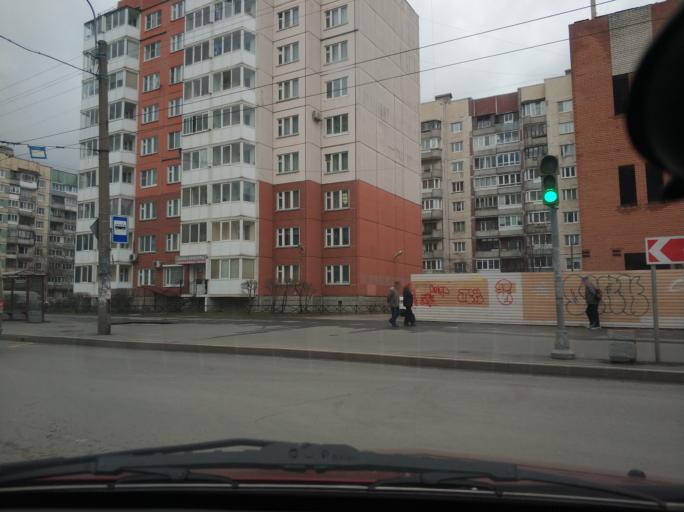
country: RU
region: St.-Petersburg
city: Krasnogvargeisky
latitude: 59.9491
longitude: 30.4813
